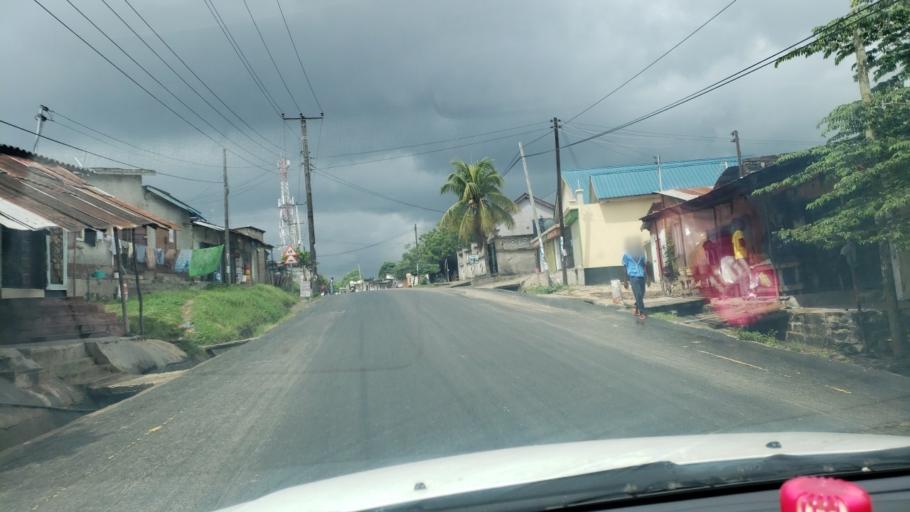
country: TZ
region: Dar es Salaam
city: Magomeni
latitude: -6.8058
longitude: 39.2442
